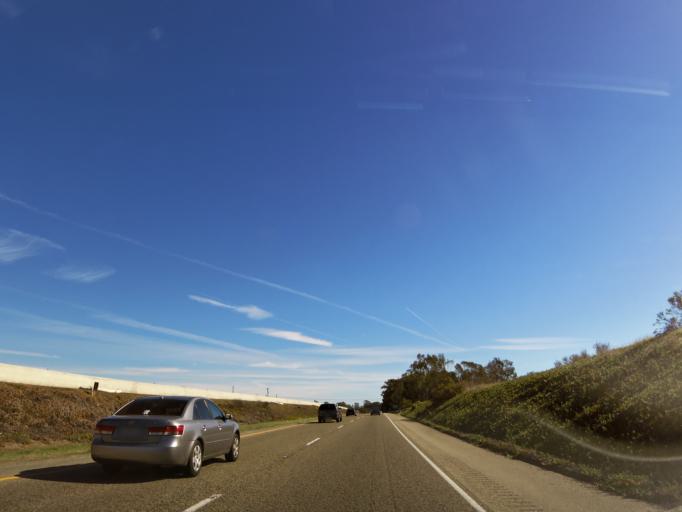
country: US
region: California
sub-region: Santa Barbara County
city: Isla Vista
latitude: 34.4377
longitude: -119.9252
